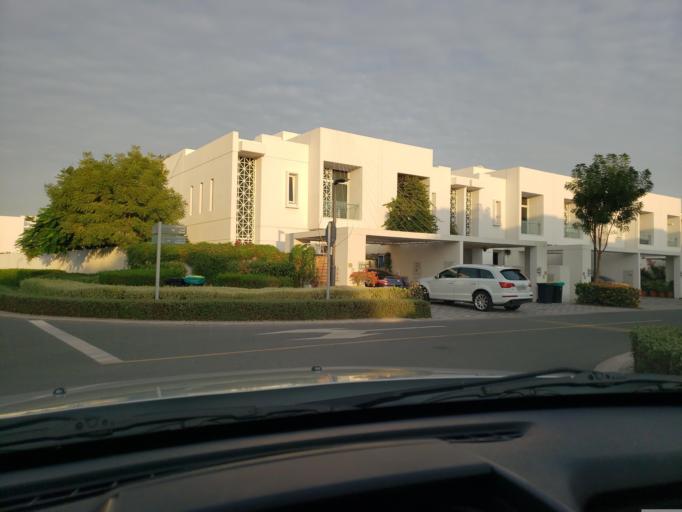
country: AE
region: Dubai
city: Dubai
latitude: 25.0151
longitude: 55.2691
